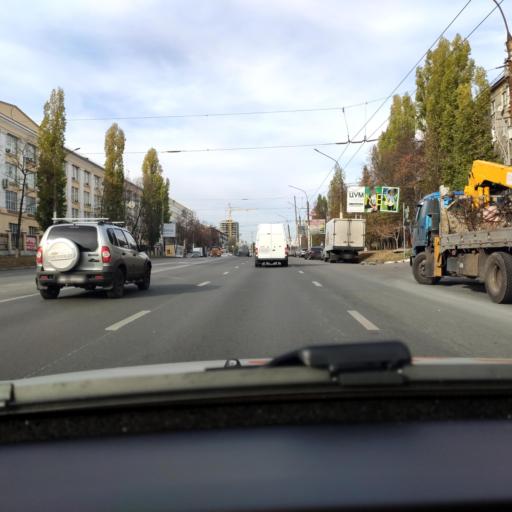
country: RU
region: Voronezj
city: Voronezh
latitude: 51.6441
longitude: 39.2008
